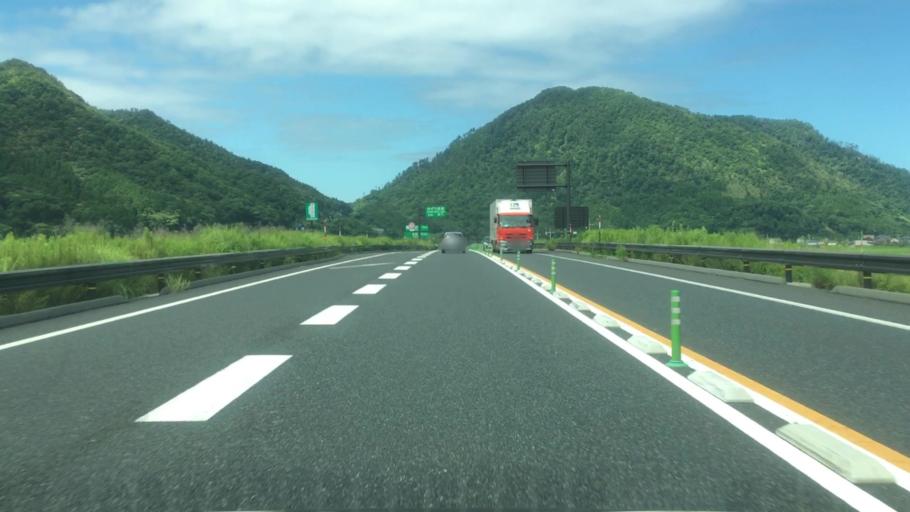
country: JP
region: Tottori
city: Tottori
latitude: 35.5713
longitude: 134.3036
